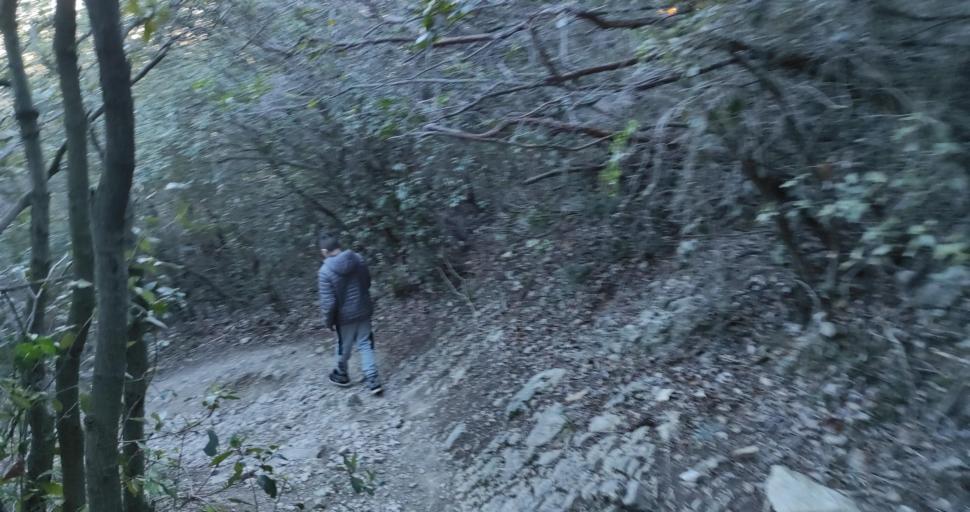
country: IT
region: The Marches
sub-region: Provincia di Ancona
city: Sirolo
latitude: 43.5441
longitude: 13.6221
